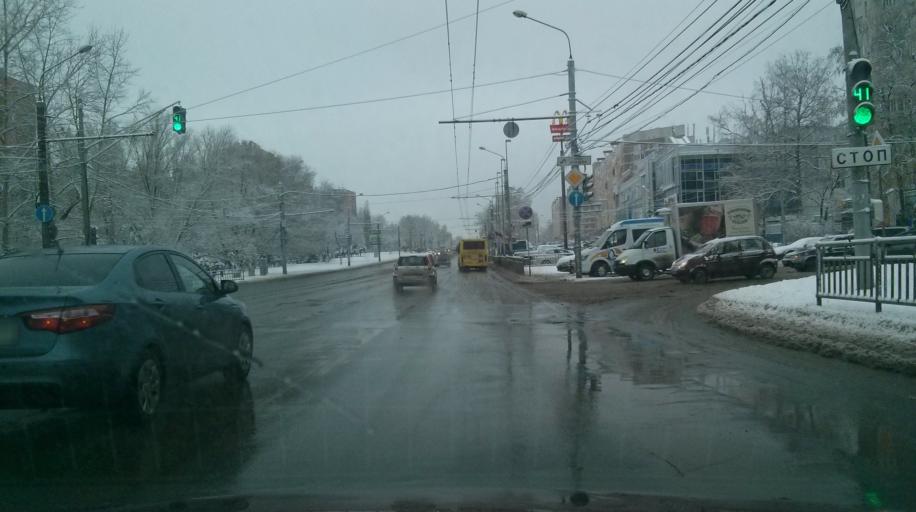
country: RU
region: Nizjnij Novgorod
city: Nizhniy Novgorod
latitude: 56.2361
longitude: 43.9541
